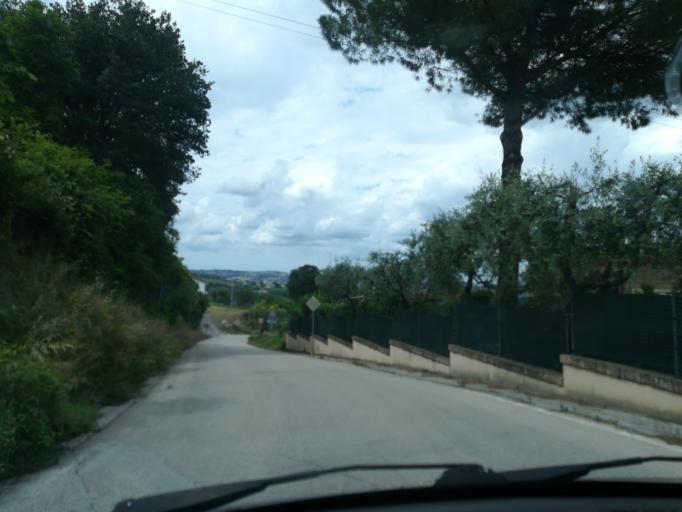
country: IT
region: The Marches
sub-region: Provincia di Macerata
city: Petriolo
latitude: 43.2252
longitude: 13.4639
